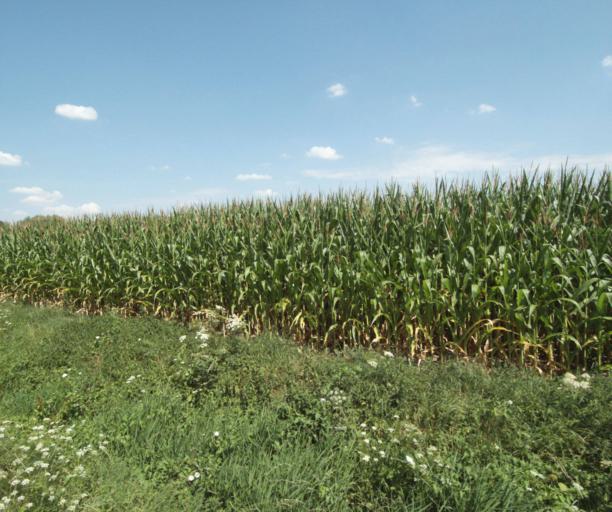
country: FR
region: Nord-Pas-de-Calais
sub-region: Departement du Nord
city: Neuville-en-Ferrain
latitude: 50.7546
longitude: 3.1713
